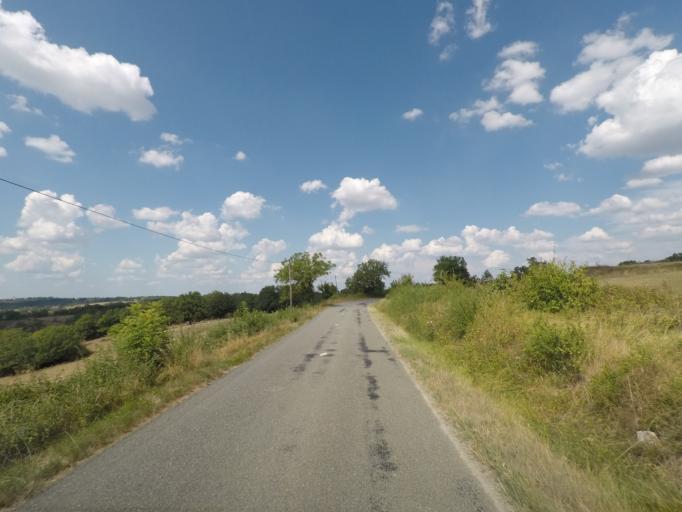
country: FR
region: Midi-Pyrenees
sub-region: Departement du Lot
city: Le Vigan
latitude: 44.6183
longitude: 1.5985
